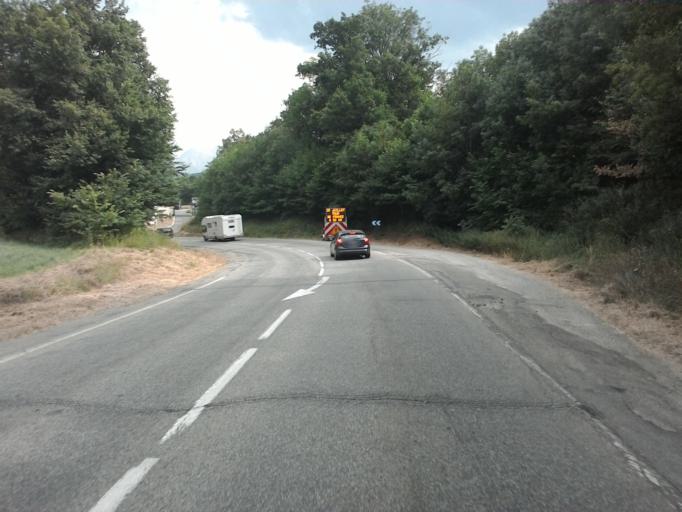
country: FR
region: Rhone-Alpes
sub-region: Departement de l'Isere
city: La Mure
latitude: 44.9000
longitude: 5.8010
